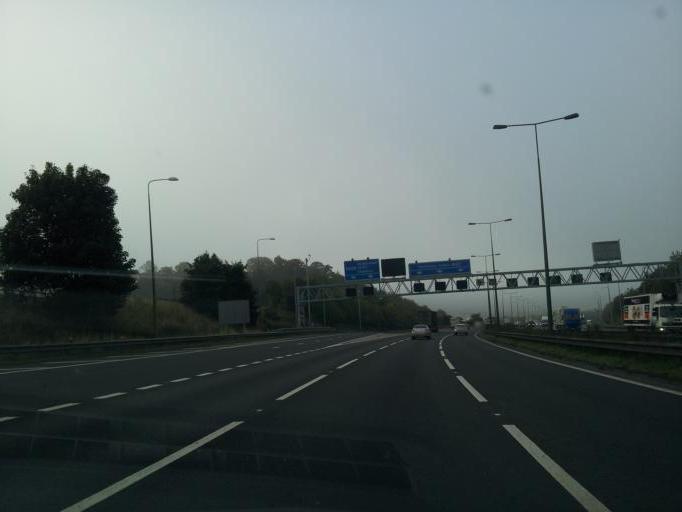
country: GB
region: England
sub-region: Calderdale
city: Brighouse
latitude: 53.6993
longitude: -1.7456
